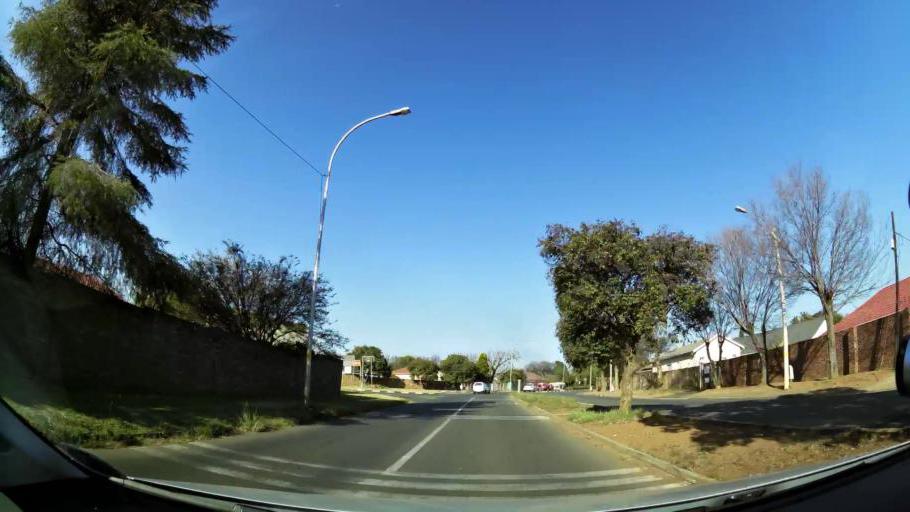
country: ZA
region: Gauteng
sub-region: City of Johannesburg Metropolitan Municipality
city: Modderfontein
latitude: -26.1516
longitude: 28.1625
